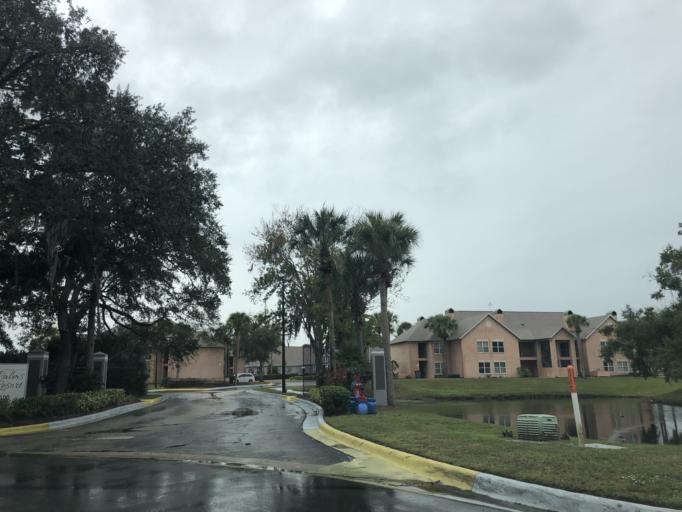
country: US
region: Florida
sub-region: Osceola County
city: Celebration
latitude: 28.3410
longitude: -81.5345
